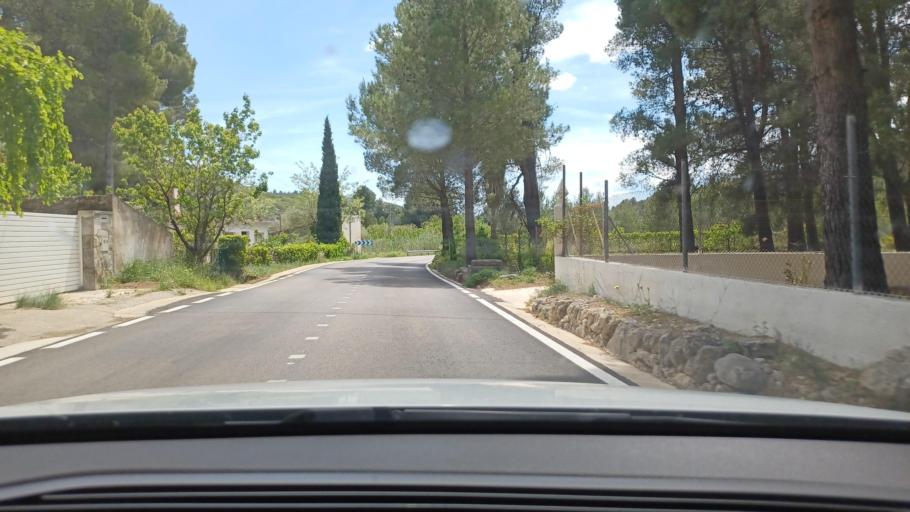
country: ES
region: Valencia
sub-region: Provincia de Castello
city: Rosell
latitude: 40.6550
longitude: 0.2678
